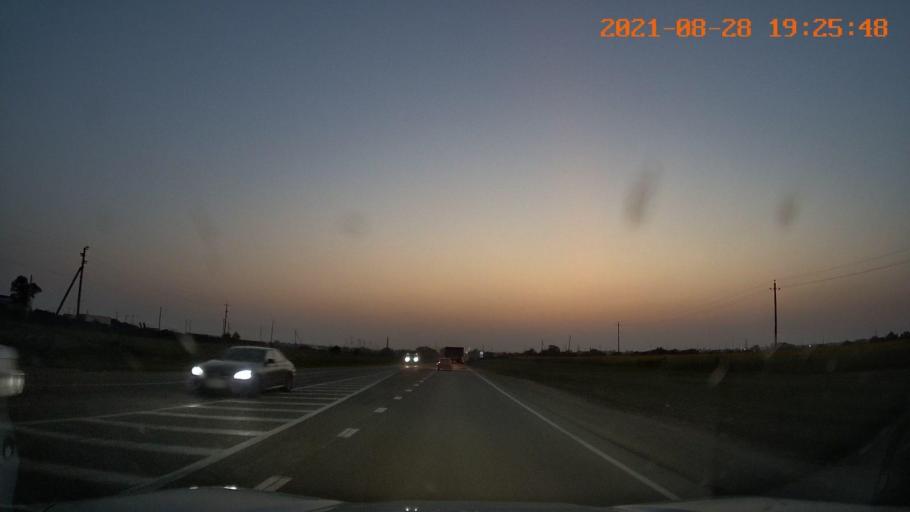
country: RU
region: Adygeya
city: Ponezhukay
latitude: 44.8780
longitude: 39.4043
